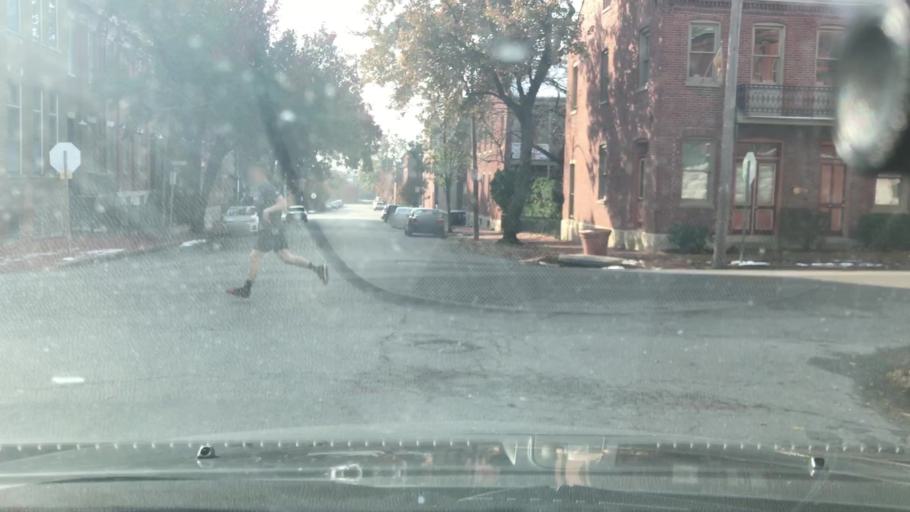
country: US
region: Missouri
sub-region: City of Saint Louis
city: St. Louis
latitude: 38.6082
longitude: -90.2033
